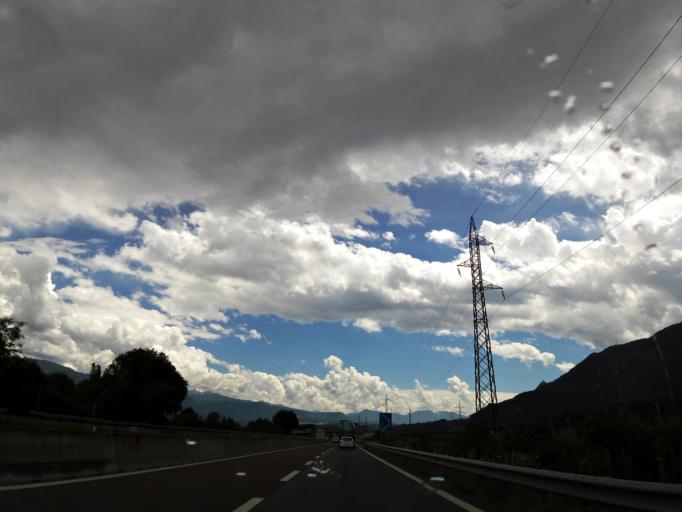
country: IT
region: Trentino-Alto Adige
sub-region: Bolzano
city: Terlano
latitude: 46.5261
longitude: 11.2425
